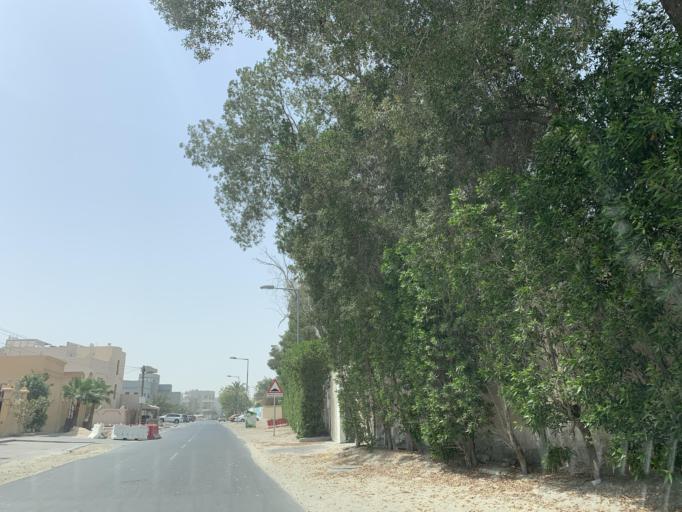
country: BH
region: Northern
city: Madinat `Isa
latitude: 26.1747
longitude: 50.5229
